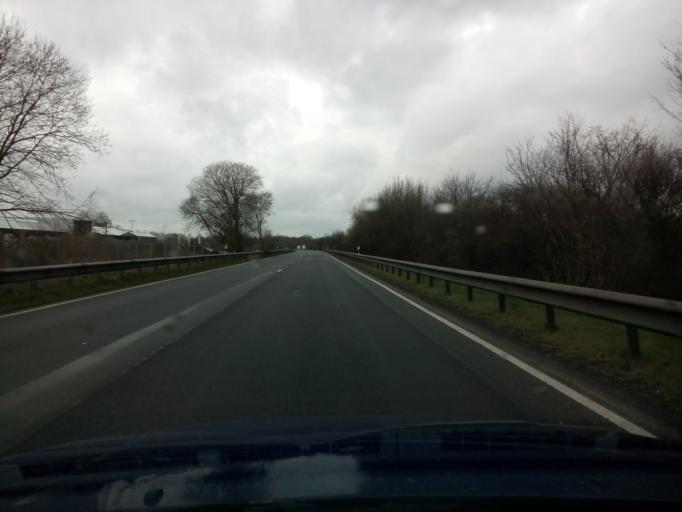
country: DE
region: Lower Saxony
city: Haselunne
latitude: 52.6857
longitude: 7.4923
